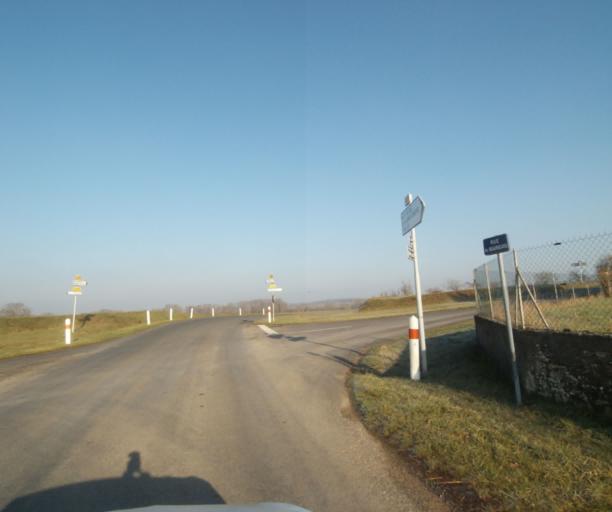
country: FR
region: Champagne-Ardenne
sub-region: Departement de la Haute-Marne
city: Montier-en-Der
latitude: 48.4142
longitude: 4.7414
